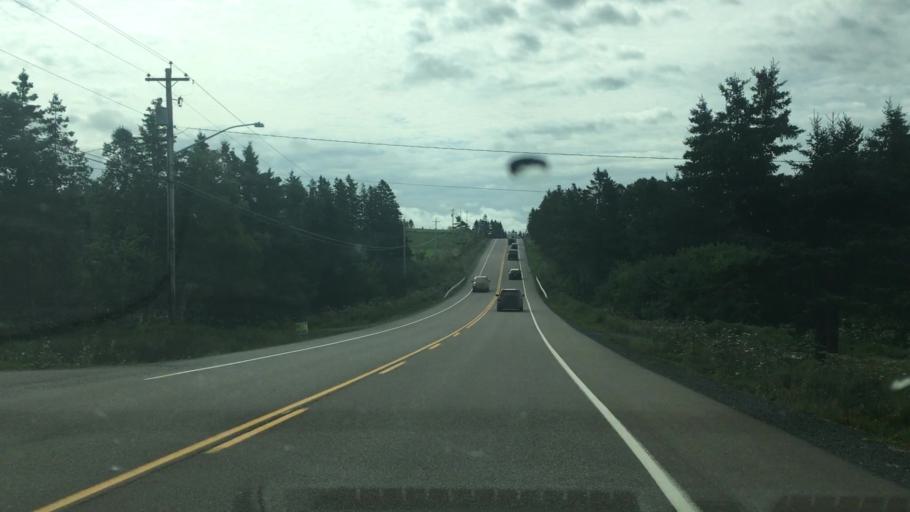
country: CA
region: Nova Scotia
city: Princeville
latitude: 45.7004
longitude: -60.7371
